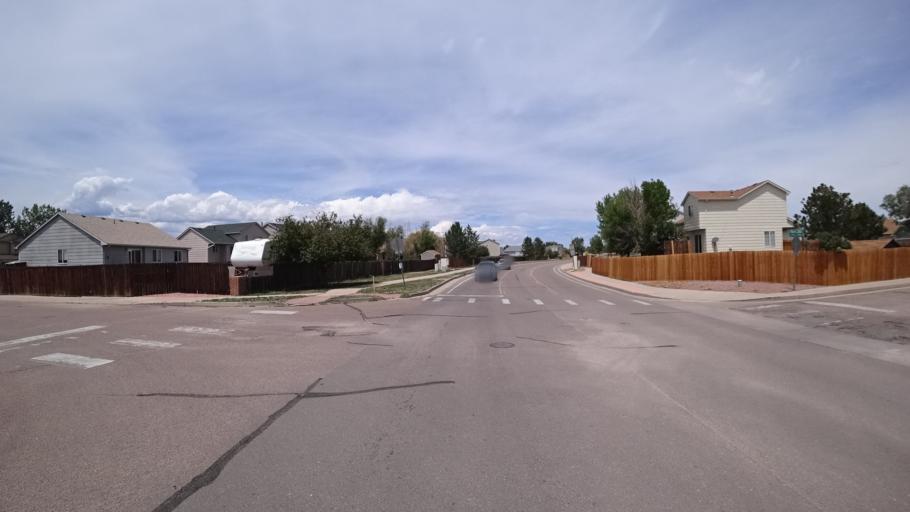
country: US
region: Colorado
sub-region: El Paso County
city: Fountain
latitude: 38.6679
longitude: -104.6823
